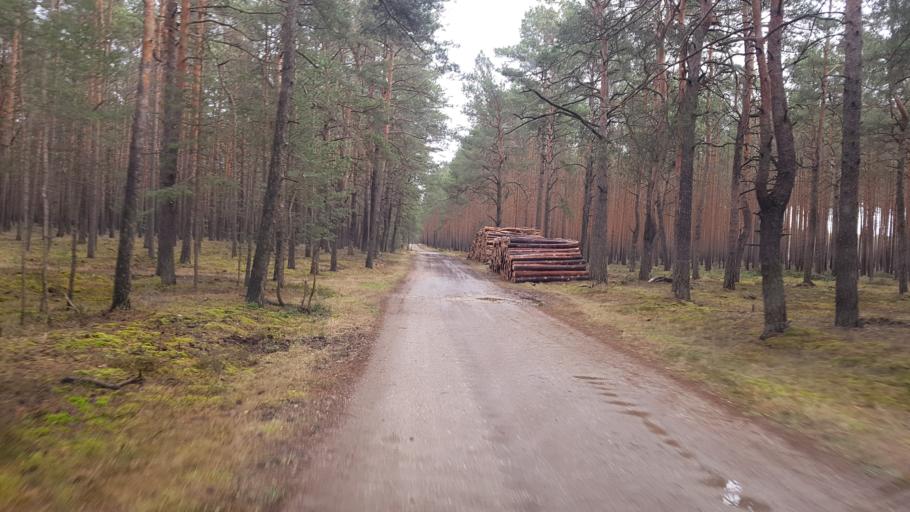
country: DE
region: Brandenburg
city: Sallgast
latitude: 51.6607
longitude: 13.8323
